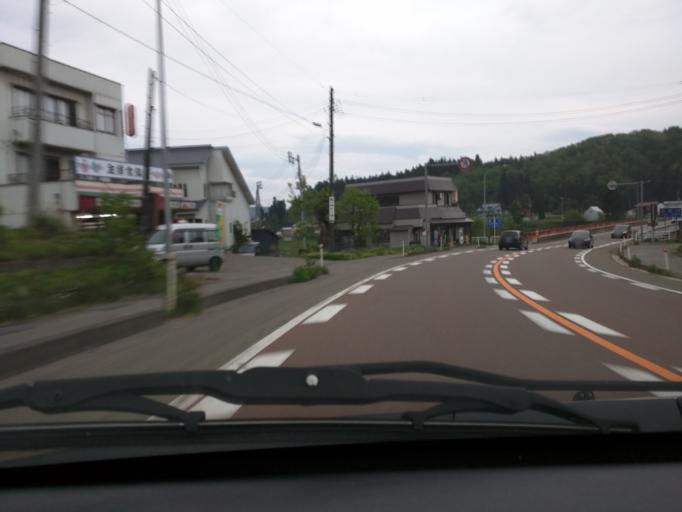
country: JP
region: Niigata
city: Ojiya
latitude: 37.2589
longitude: 138.8794
